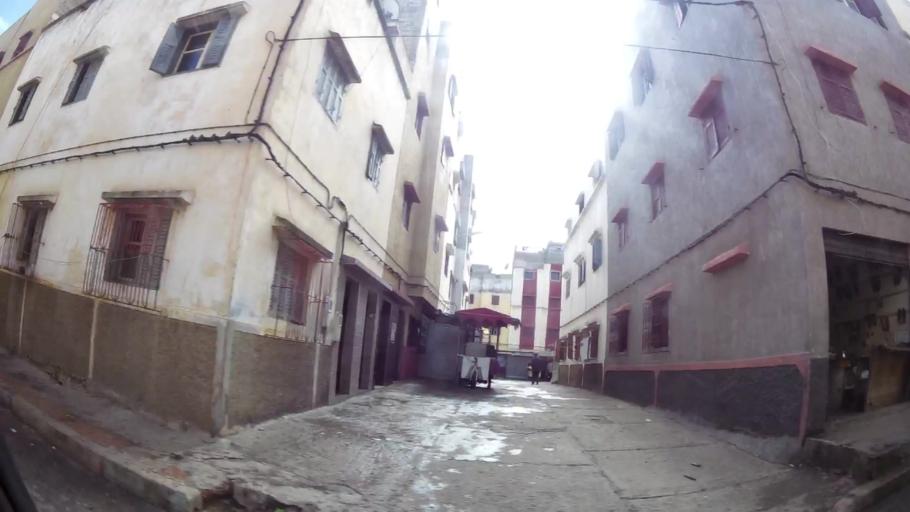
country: MA
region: Grand Casablanca
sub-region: Mohammedia
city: Mohammedia
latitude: 33.6754
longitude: -7.3872
